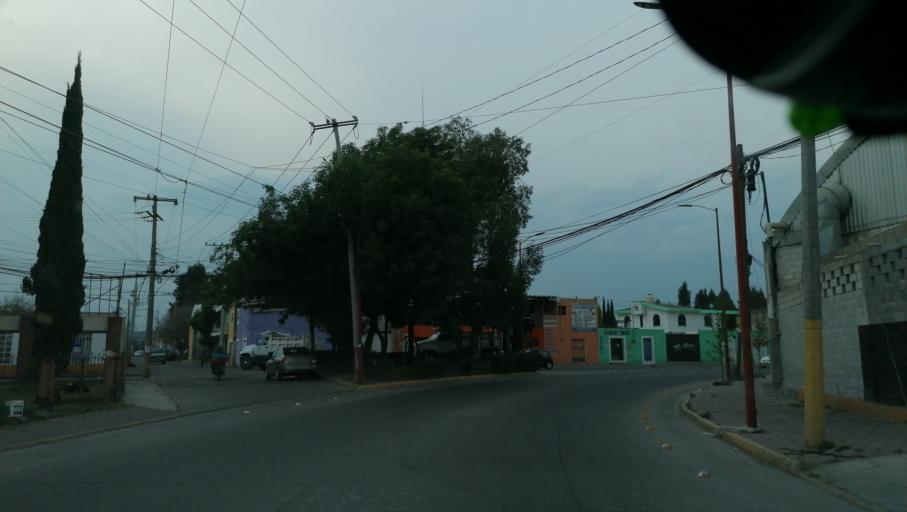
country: MX
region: Puebla
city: San Andres Cholula
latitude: 19.0495
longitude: -98.3128
